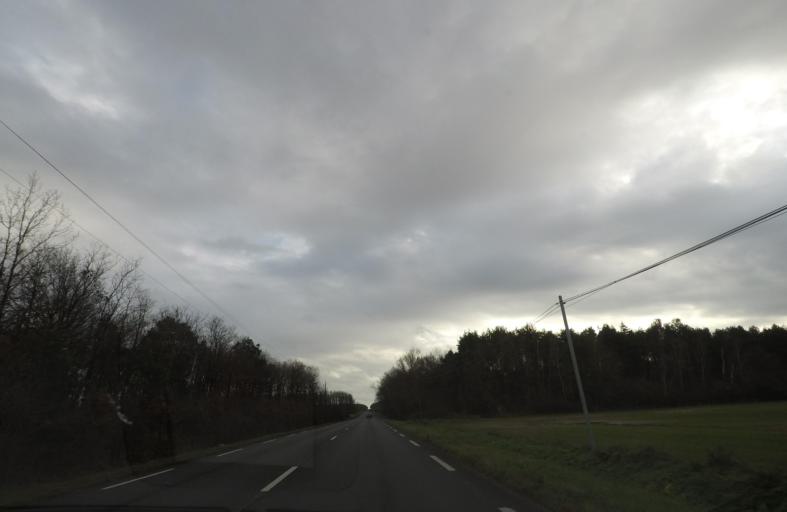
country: FR
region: Centre
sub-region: Departement du Loir-et-Cher
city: Mur-de-Sologne
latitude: 47.4280
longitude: 1.5718
